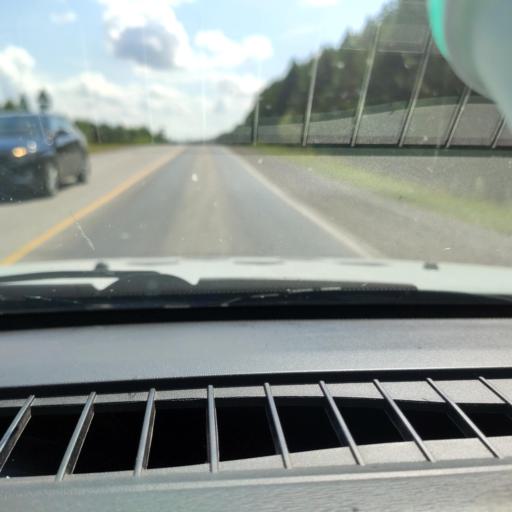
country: RU
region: Chelyabinsk
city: Mezhevoy
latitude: 55.3159
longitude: 58.7296
